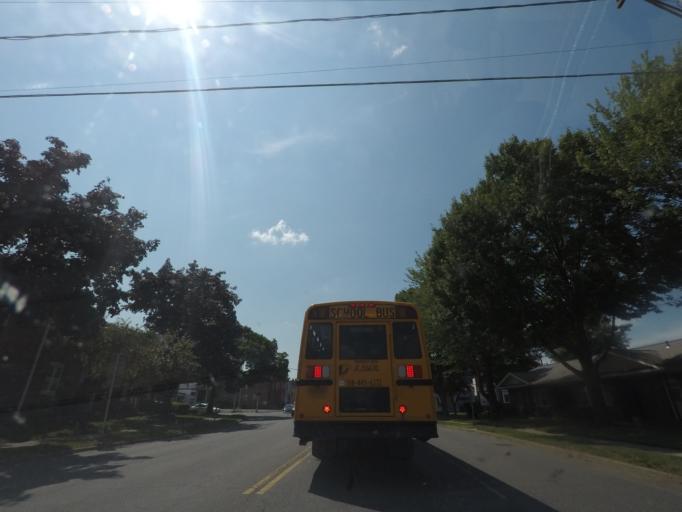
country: US
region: New York
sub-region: Albany County
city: Watervliet
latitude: 42.7328
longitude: -73.7004
